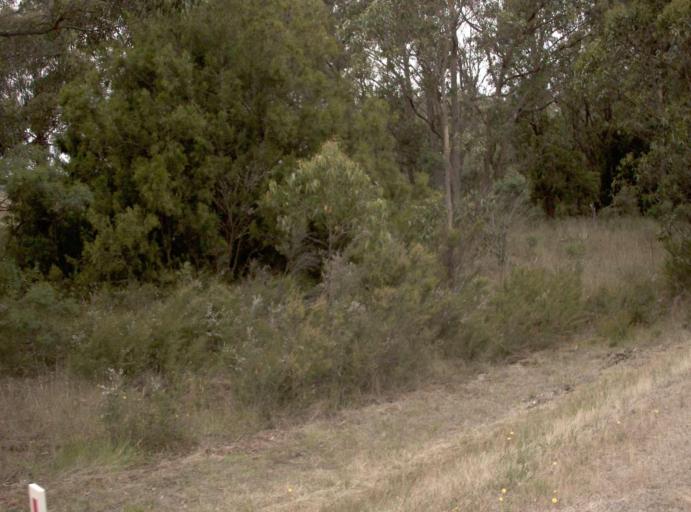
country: AU
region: Victoria
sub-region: Latrobe
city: Traralgon
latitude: -38.4969
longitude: 146.8324
